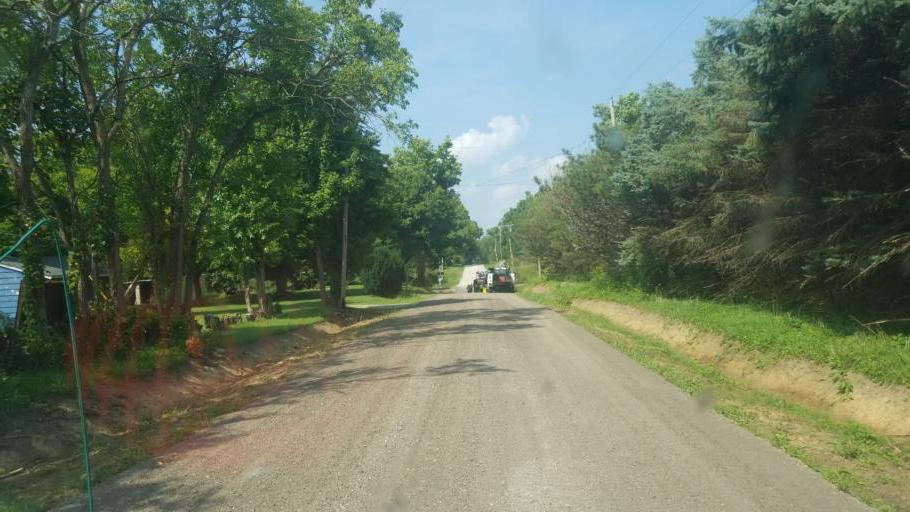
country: US
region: Ohio
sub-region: Huron County
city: New London
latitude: 41.0564
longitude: -82.4096
